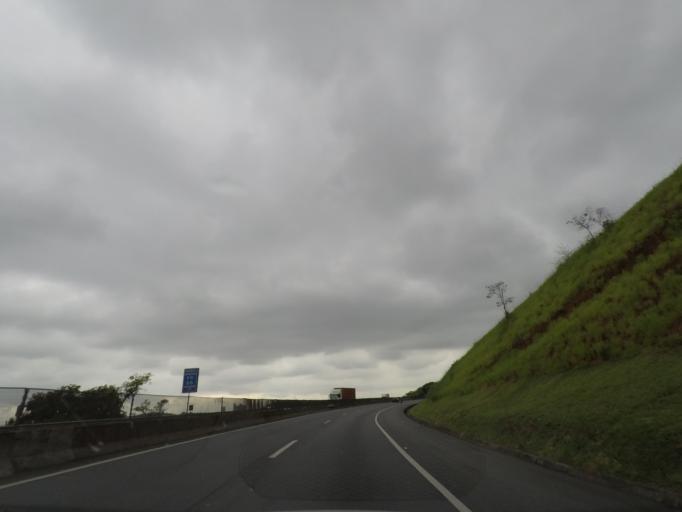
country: BR
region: Sao Paulo
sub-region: Guaratingueta
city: Guaratingueta
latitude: -22.8227
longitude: -45.2021
